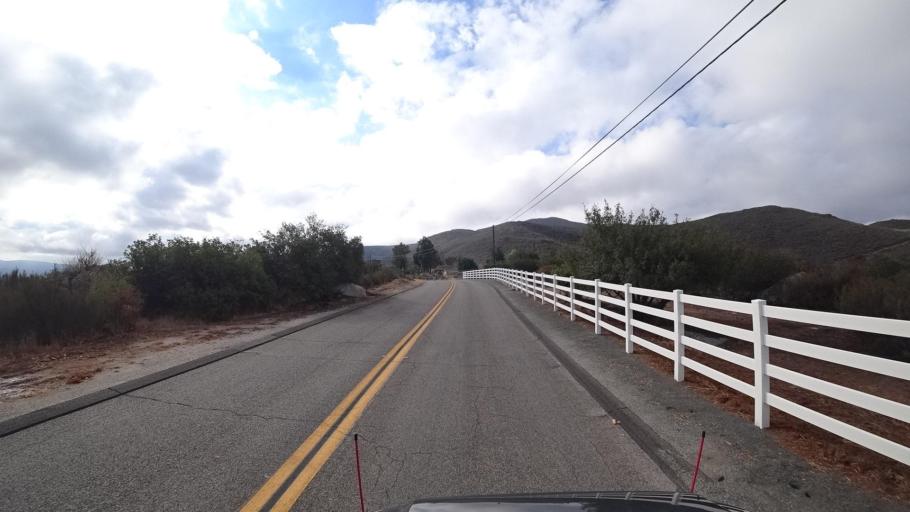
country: MX
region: Baja California
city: Tecate
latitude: 32.6322
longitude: -116.6350
